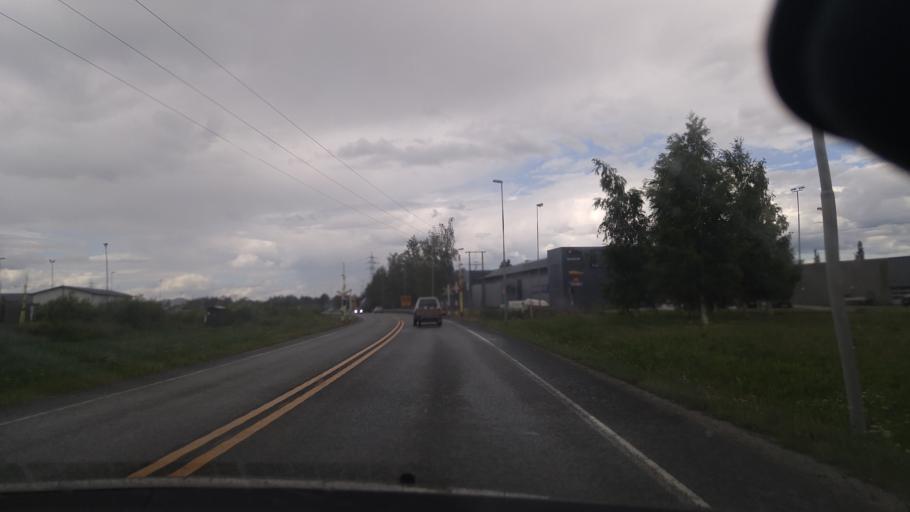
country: NO
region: Nord-Trondelag
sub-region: Verdal
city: Verdal
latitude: 63.7803
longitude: 11.4713
